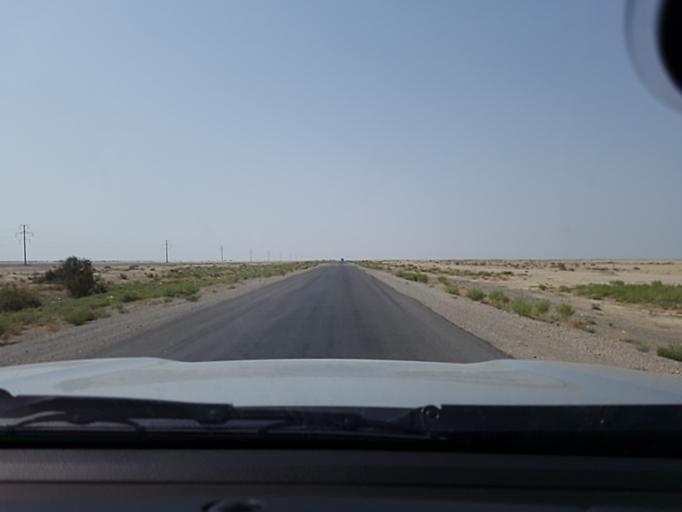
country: TM
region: Balkan
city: Gumdag
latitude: 38.8809
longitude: 54.5935
